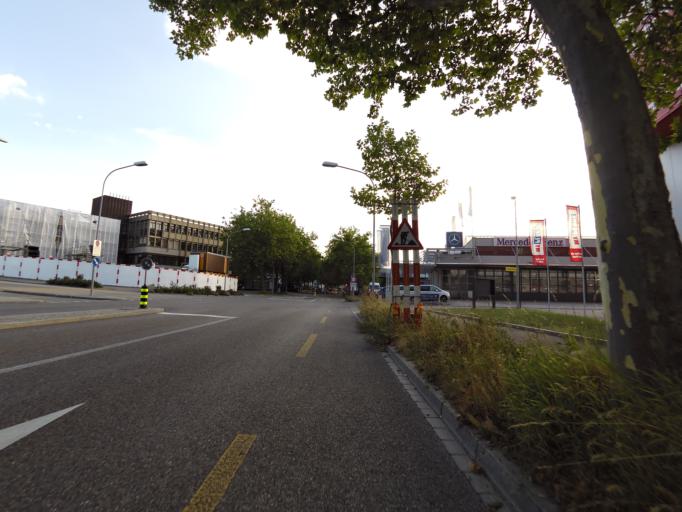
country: CH
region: Zurich
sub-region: Bezirk Zuerich
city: Zuerich (Kreis 12) / Saatlen
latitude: 47.4159
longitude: 8.5637
